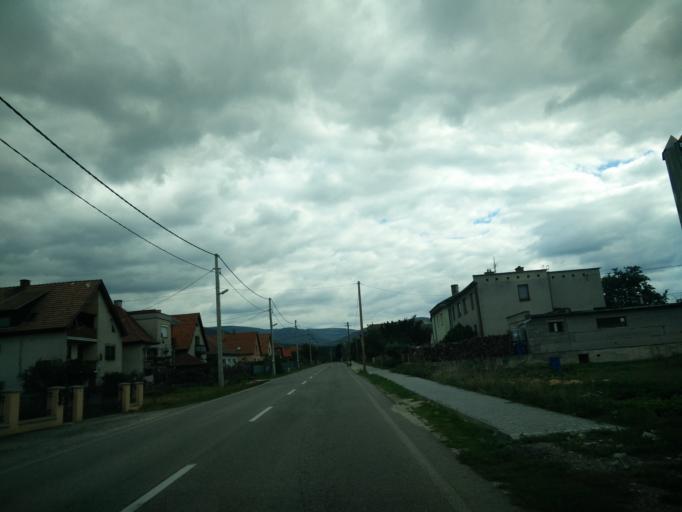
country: SK
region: Nitriansky
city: Partizanske
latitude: 48.6110
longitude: 18.4852
